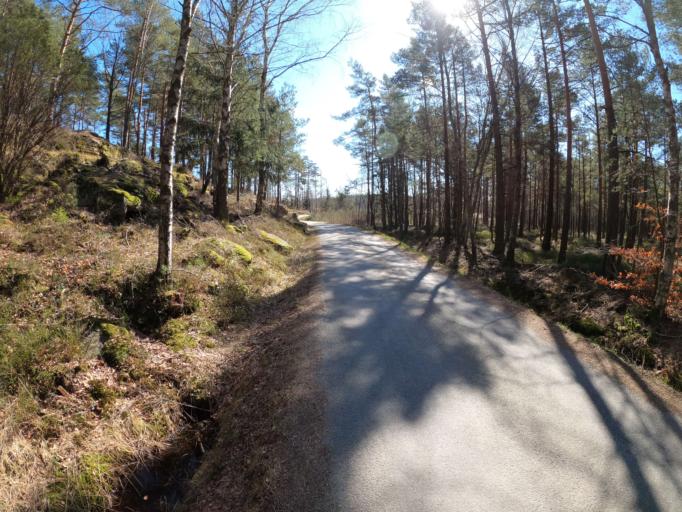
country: SE
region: Vaestra Goetaland
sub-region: Harryda Kommun
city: Molnlycke
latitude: 57.6326
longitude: 12.1192
